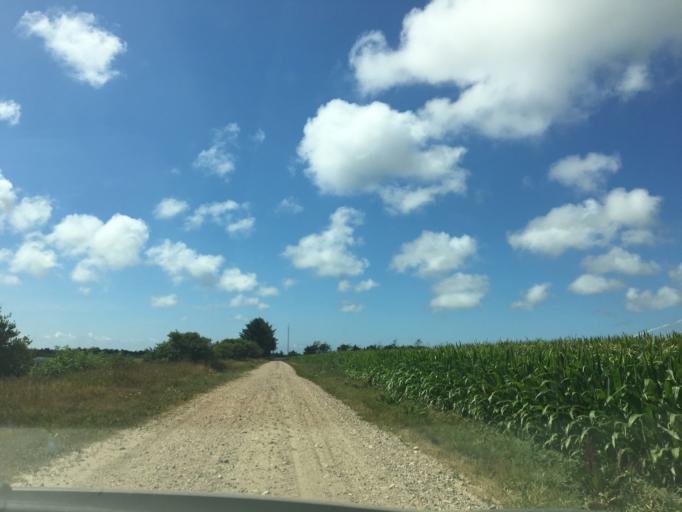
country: DK
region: South Denmark
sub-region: Varde Kommune
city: Oksbol
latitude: 55.8136
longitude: 8.2811
